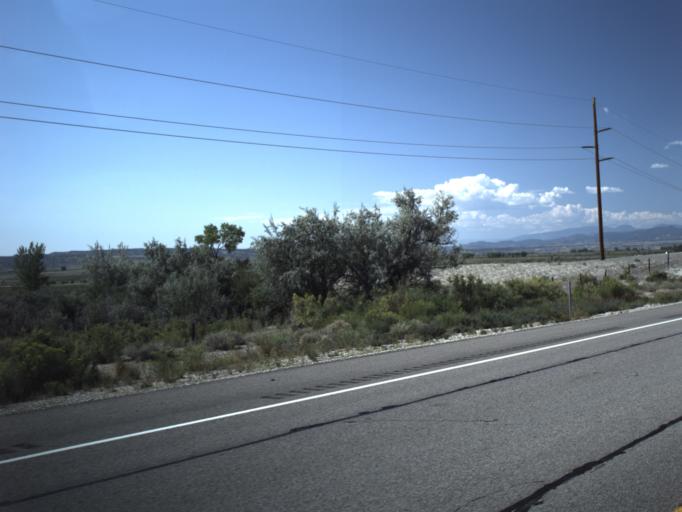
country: US
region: Utah
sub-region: Emery County
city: Ferron
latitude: 38.9313
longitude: -111.2329
